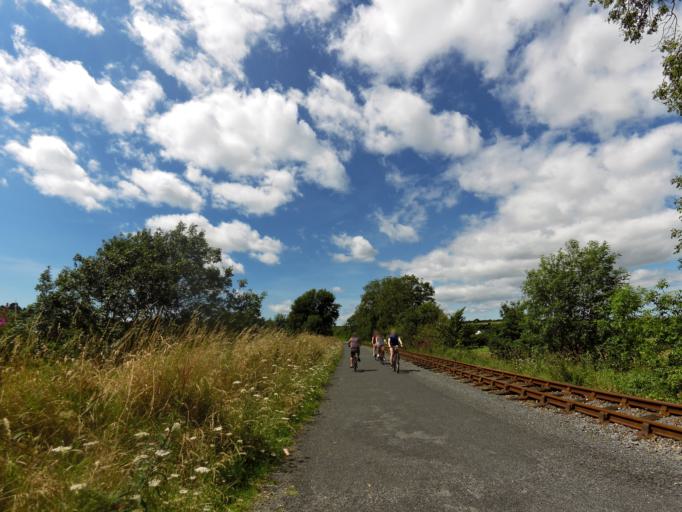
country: IE
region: Leinster
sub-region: Kilkenny
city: Mooncoin
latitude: 52.2468
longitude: -7.2330
